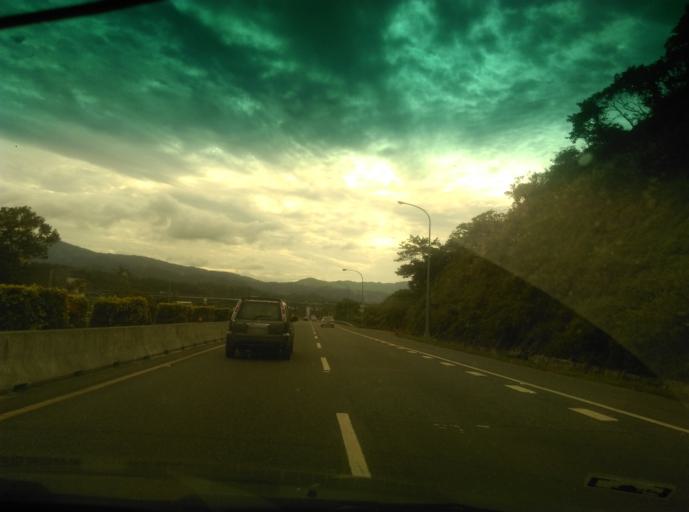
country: TW
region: Taiwan
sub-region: Keelung
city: Keelung
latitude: 25.1116
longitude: 121.7268
